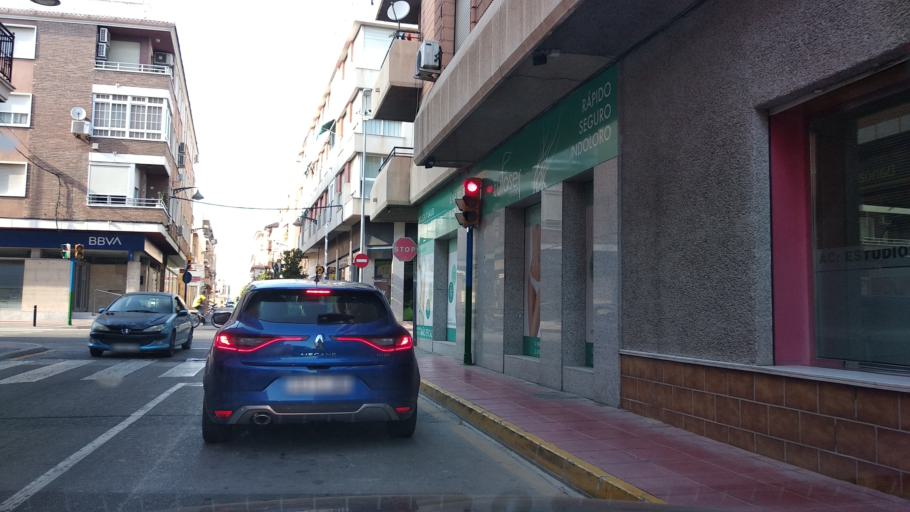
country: ES
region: Murcia
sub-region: Murcia
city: Santomera
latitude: 38.0596
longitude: -1.0480
